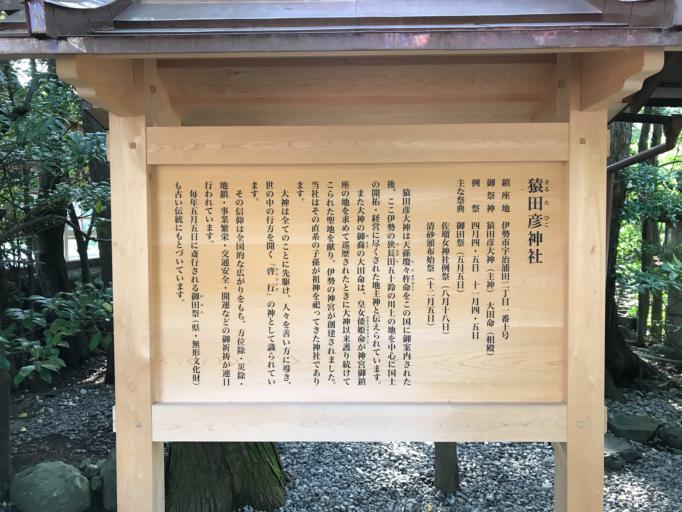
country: JP
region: Mie
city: Ise
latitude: 34.4666
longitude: 136.7204
